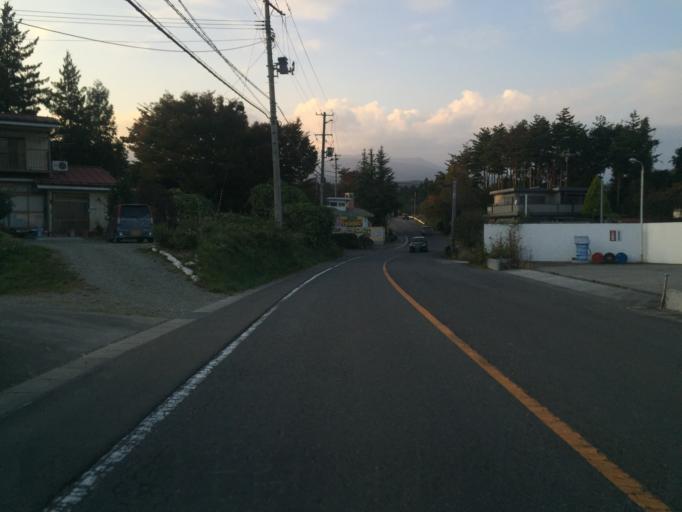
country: JP
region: Fukushima
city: Motomiya
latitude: 37.5569
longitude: 140.3551
